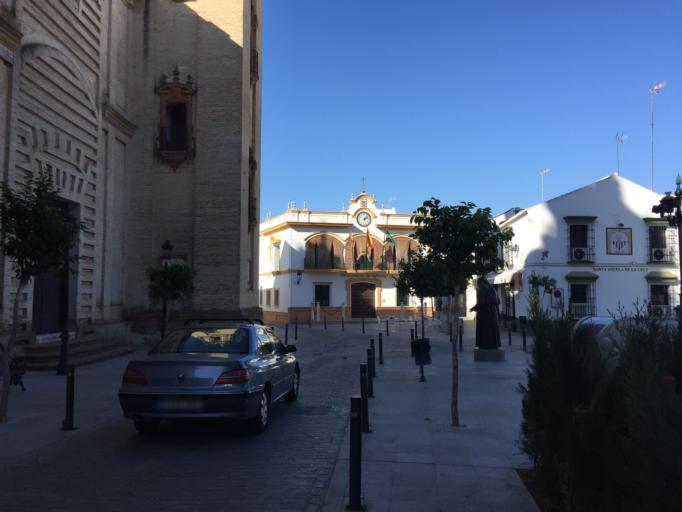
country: ES
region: Andalusia
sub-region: Provincia de Sevilla
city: Umbrete
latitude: 37.3700
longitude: -6.1574
